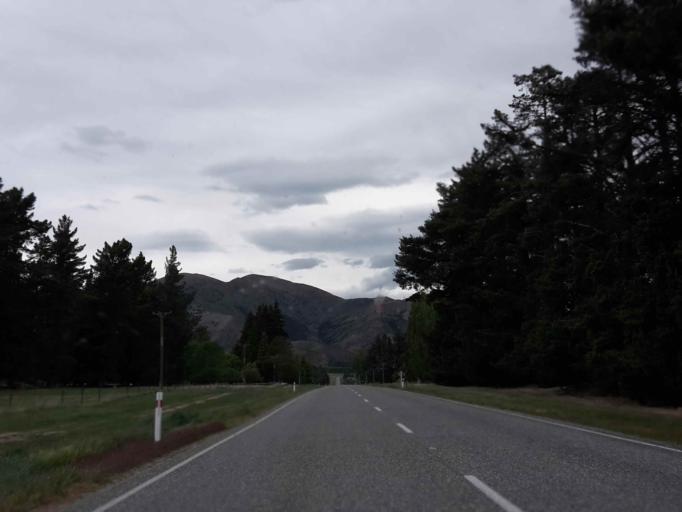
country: NZ
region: Otago
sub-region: Queenstown-Lakes District
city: Wanaka
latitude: -44.7335
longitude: 169.3141
